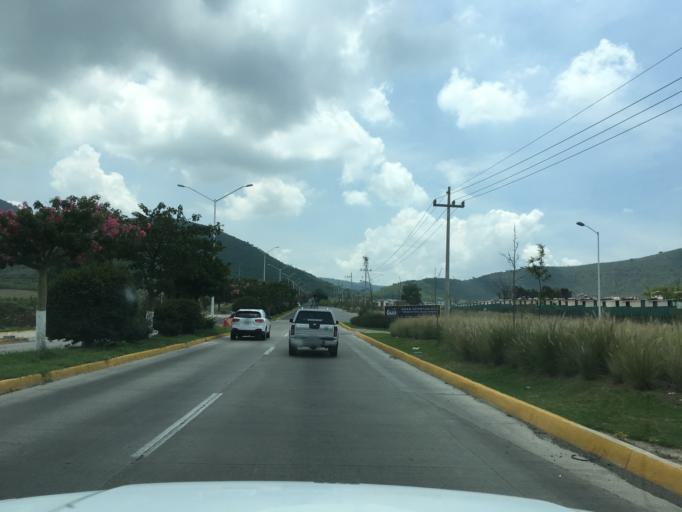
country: MX
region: Jalisco
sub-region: Tlajomulco de Zuniga
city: Santa Cruz de las Flores
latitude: 20.4905
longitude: -103.4820
